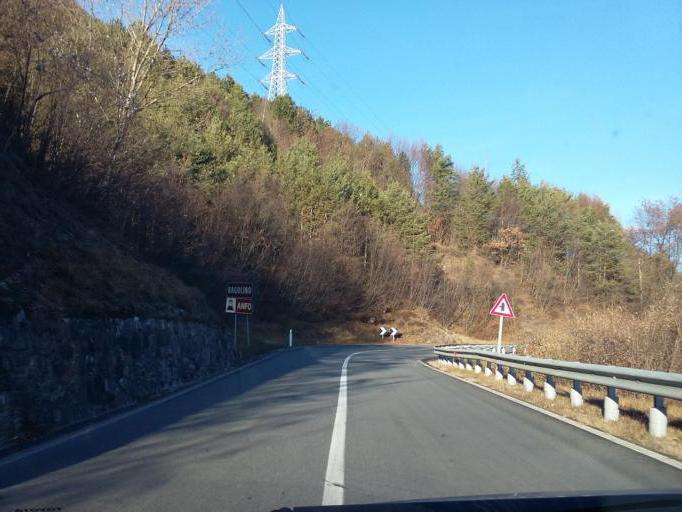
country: IT
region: Lombardy
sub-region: Provincia di Brescia
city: Ponte Caffaro
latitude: 45.8071
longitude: 10.5075
